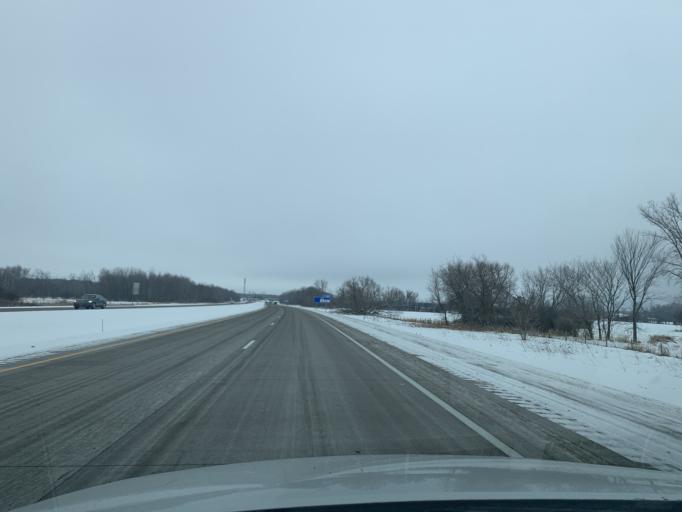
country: US
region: Minnesota
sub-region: Chisago County
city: Rush City
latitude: 45.6947
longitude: -92.9923
